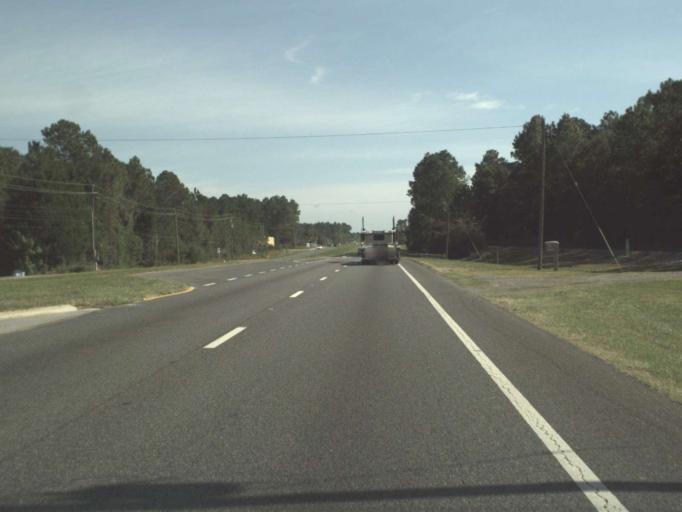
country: US
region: Florida
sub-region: Bay County
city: Hiland Park
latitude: 30.2625
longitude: -85.5376
